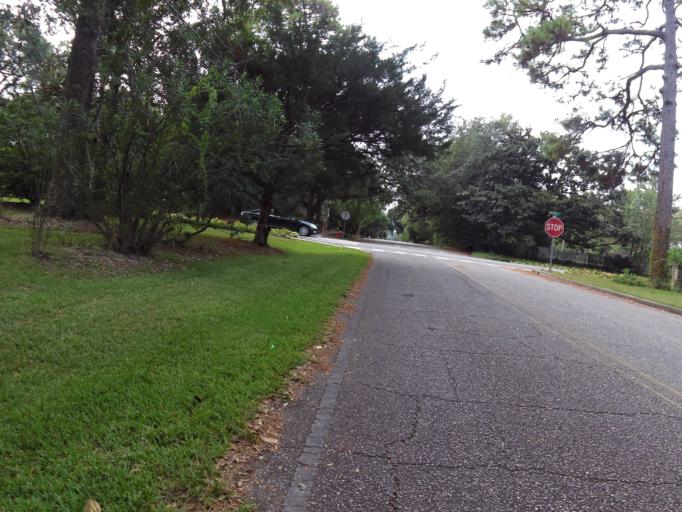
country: US
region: Alabama
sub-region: Baldwin County
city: Fairhope
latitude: 30.5248
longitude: -87.9063
